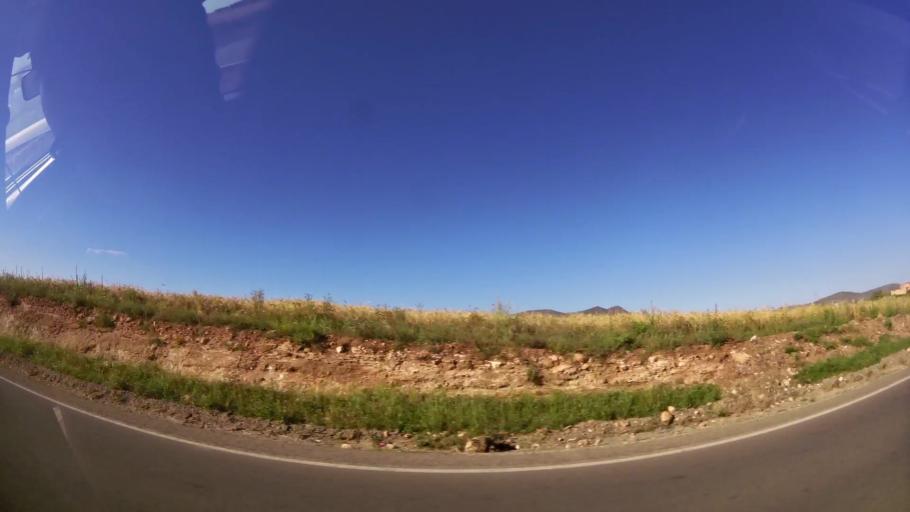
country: MA
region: Oriental
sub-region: Berkane-Taourirt
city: Ahfir
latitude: 34.9763
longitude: -2.1310
